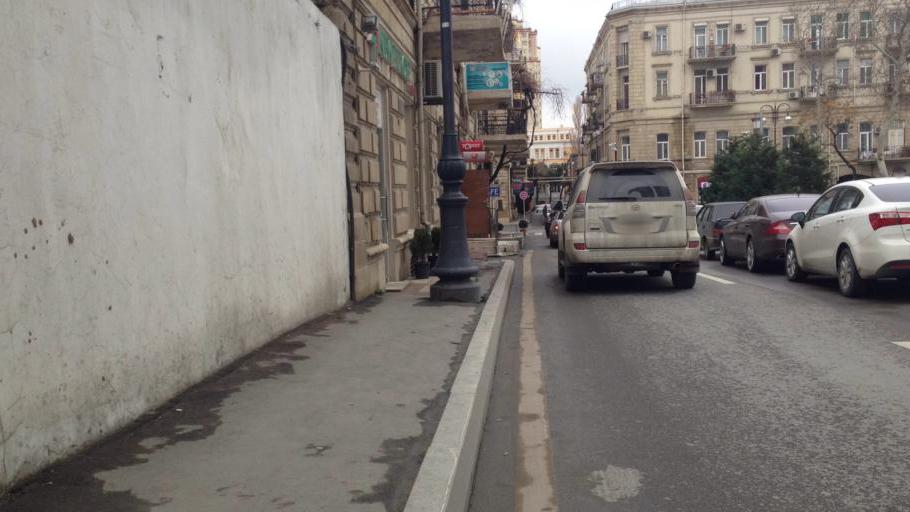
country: AZ
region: Baki
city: Baku
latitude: 40.3768
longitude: 49.8419
